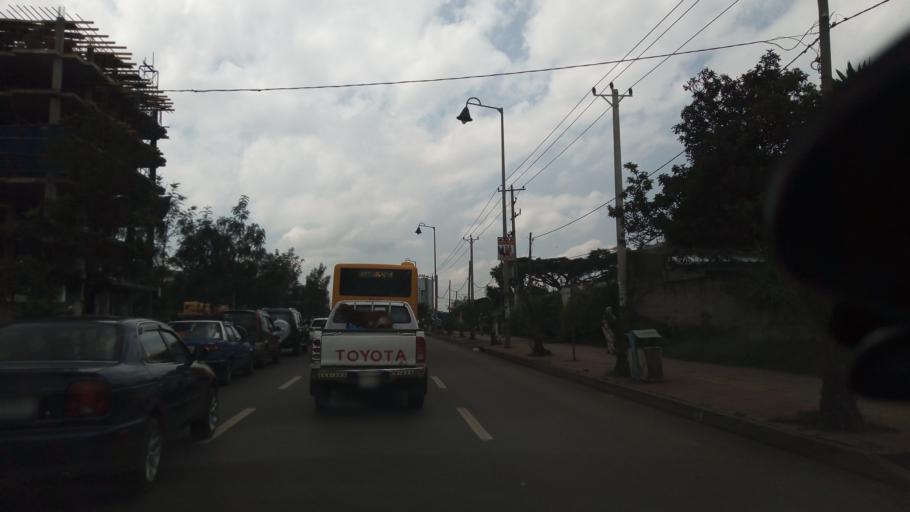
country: ET
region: Adis Abeba
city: Addis Ababa
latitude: 8.9909
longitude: 38.7198
